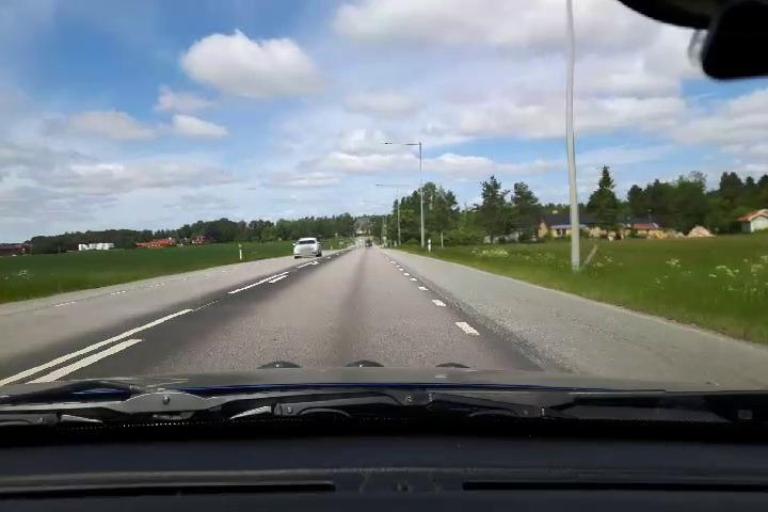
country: SE
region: Uppsala
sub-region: Osthammars Kommun
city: Bjorklinge
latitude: 60.0208
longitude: 17.5553
